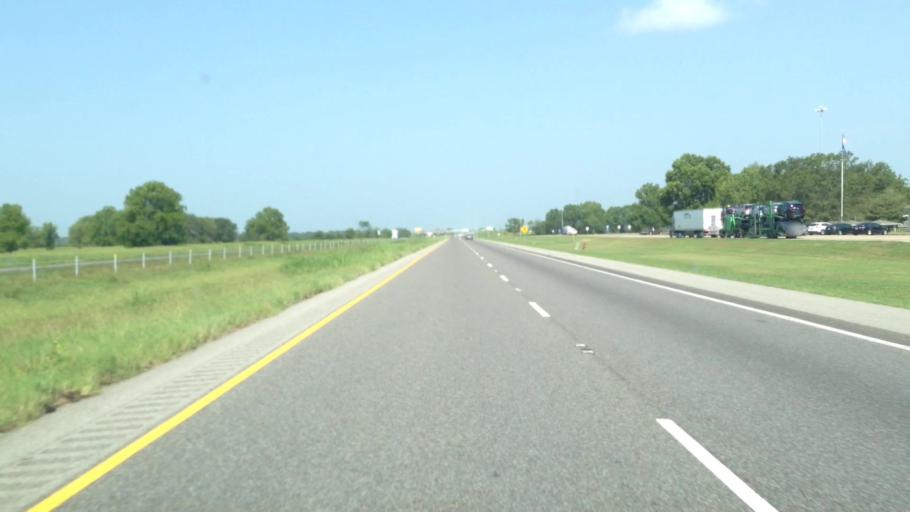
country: US
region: Mississippi
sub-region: Warren County
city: Vicksburg
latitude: 32.3244
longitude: -90.9885
